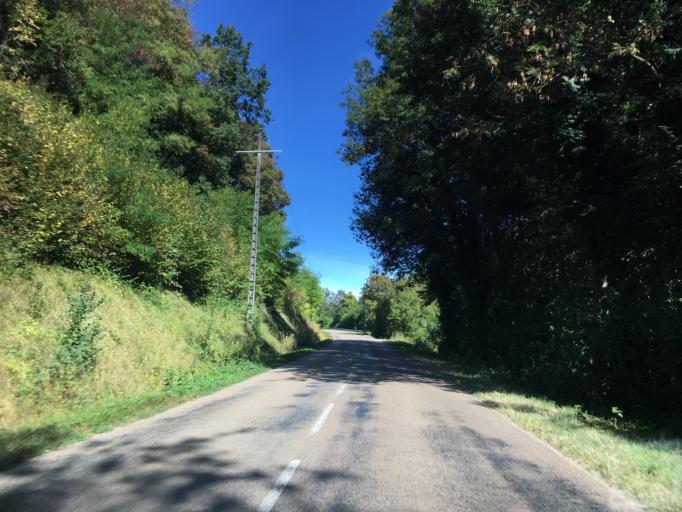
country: FR
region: Bourgogne
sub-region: Departement de l'Yonne
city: Vermenton
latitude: 47.6472
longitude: 3.6594
